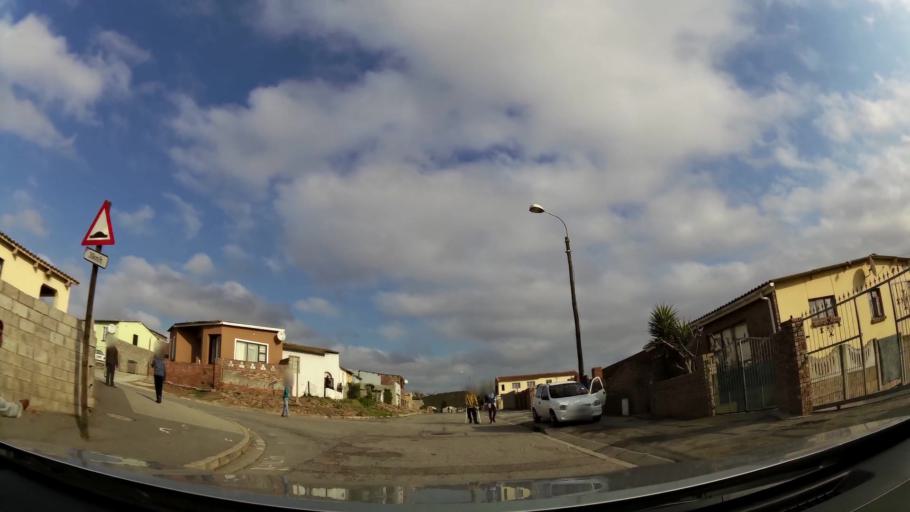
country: ZA
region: Eastern Cape
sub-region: Nelson Mandela Bay Metropolitan Municipality
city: Port Elizabeth
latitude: -33.9177
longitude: 25.5473
